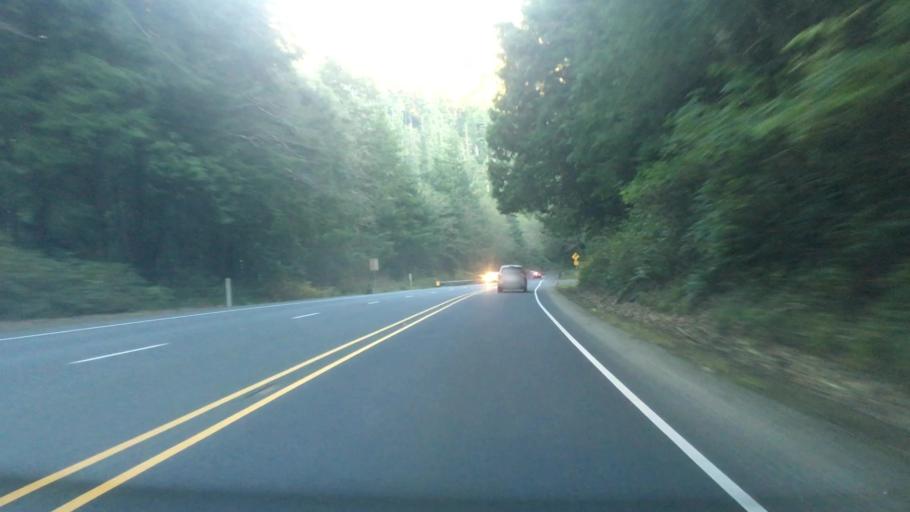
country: US
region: Oregon
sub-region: Clatsop County
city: Cannon Beach
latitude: 45.7757
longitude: -123.9460
